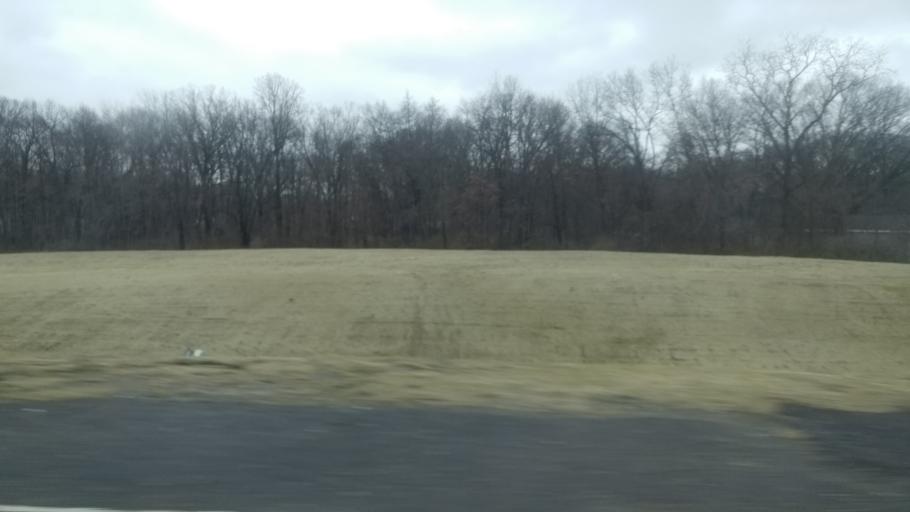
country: US
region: Ohio
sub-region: Lucas County
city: Sylvania
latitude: 41.6749
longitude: -83.6958
